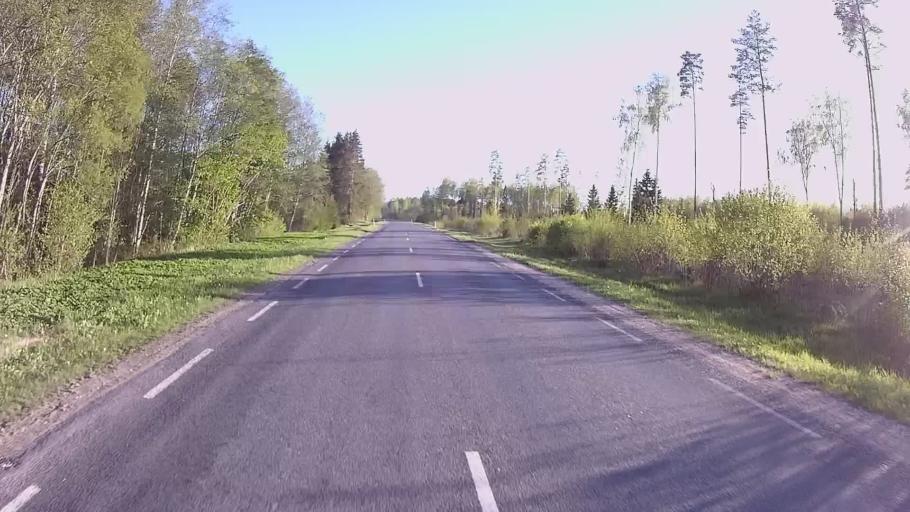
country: EE
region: Viljandimaa
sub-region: Viiratsi vald
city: Viiratsi
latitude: 58.4495
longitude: 25.7401
